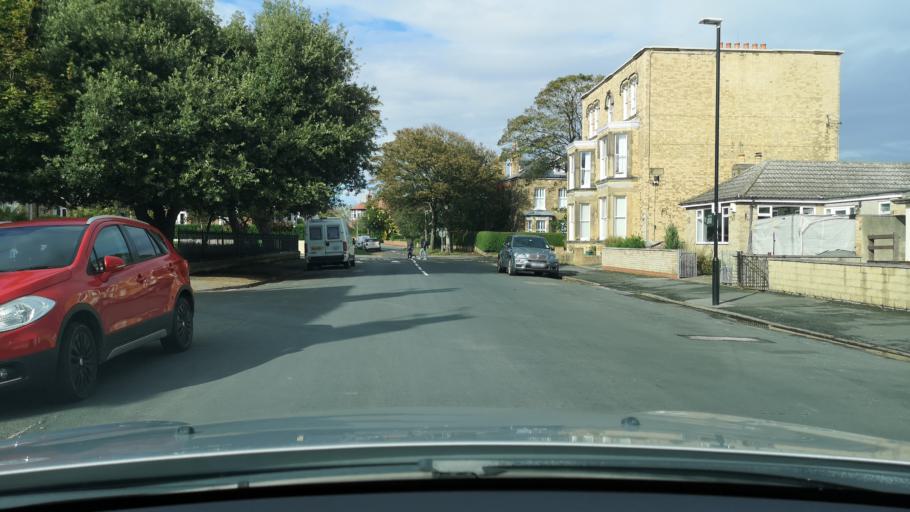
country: GB
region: England
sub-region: East Riding of Yorkshire
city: Hornsea
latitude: 53.9123
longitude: -0.1638
